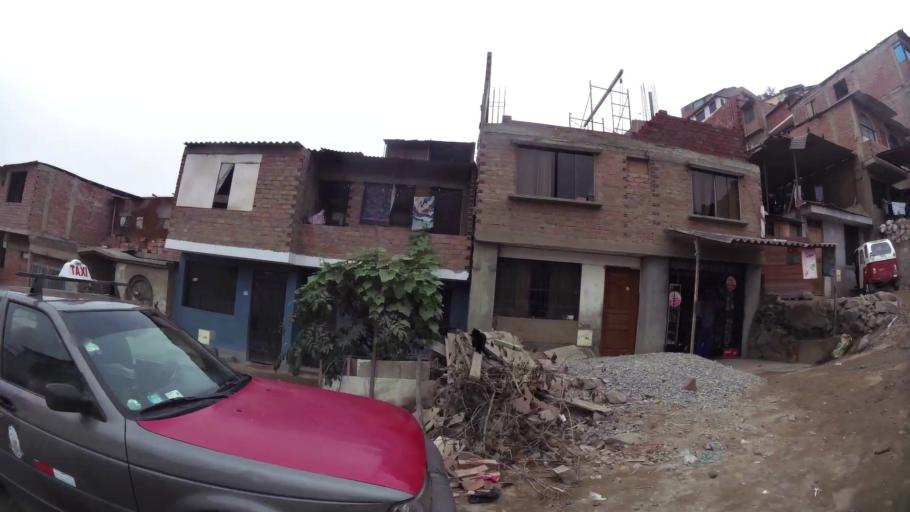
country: PE
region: Lima
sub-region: Lima
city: Surco
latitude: -12.1763
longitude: -76.9523
